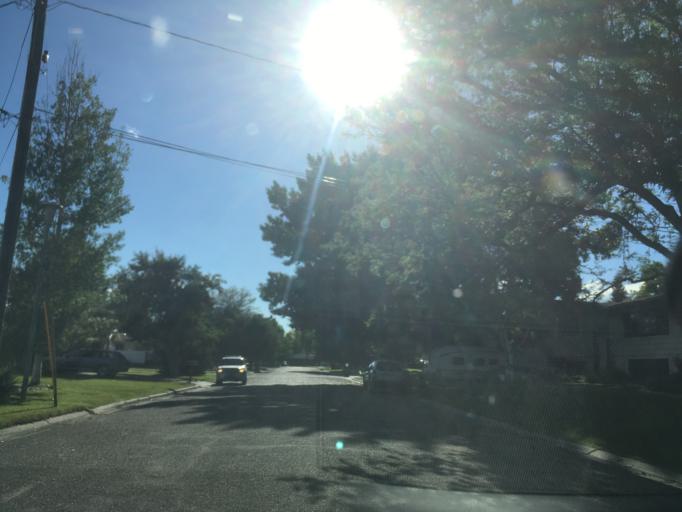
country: US
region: Montana
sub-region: Yellowstone County
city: Billings
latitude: 45.7938
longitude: -108.5612
